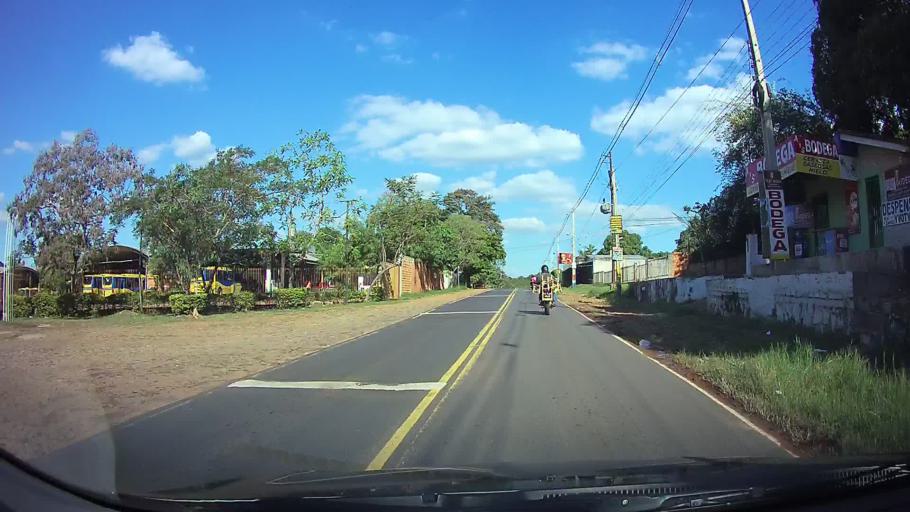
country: PY
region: Central
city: Limpio
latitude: -25.2207
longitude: -57.4786
